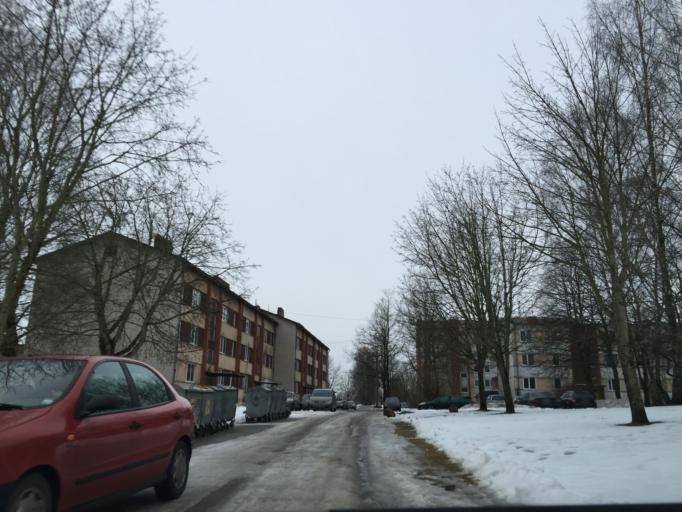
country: LV
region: Krimulda
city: Ragana
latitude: 57.1817
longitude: 24.7036
